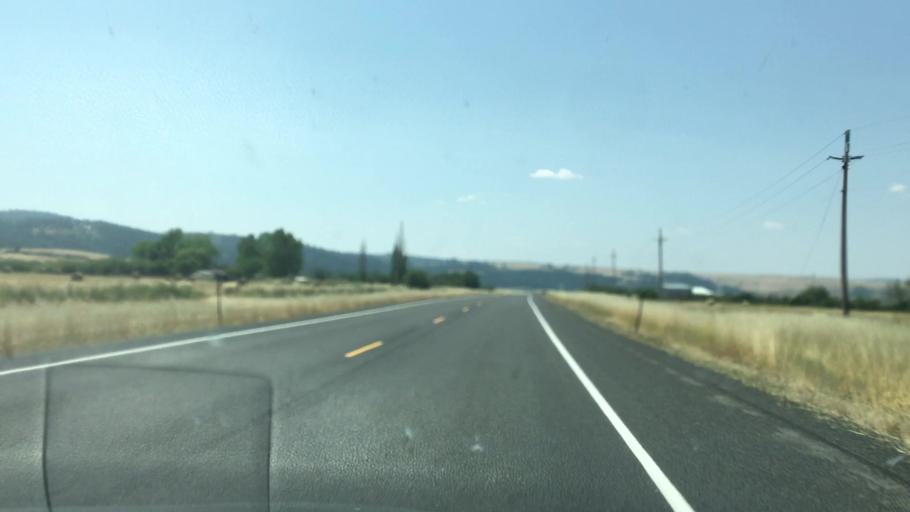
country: US
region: Idaho
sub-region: Idaho County
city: Grangeville
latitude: 45.8994
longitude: -116.1812
